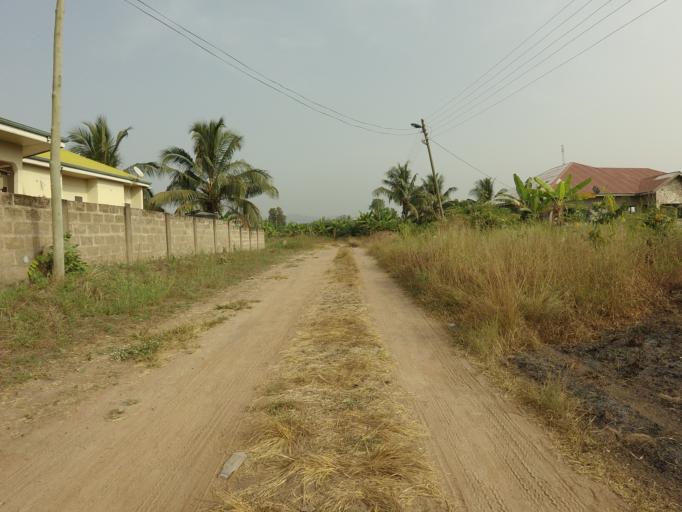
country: GH
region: Volta
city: Ho
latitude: 6.6011
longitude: 0.4865
